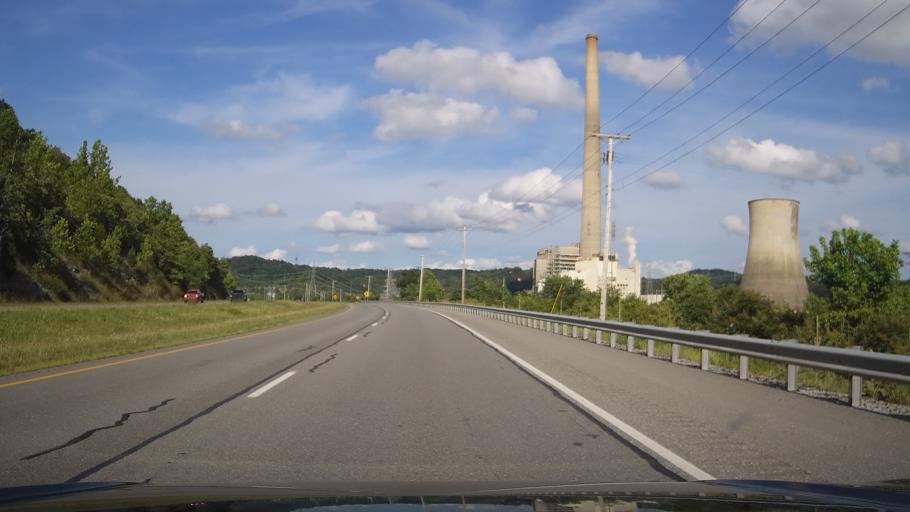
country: US
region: Kentucky
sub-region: Lawrence County
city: Louisa
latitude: 38.1718
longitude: -82.6262
